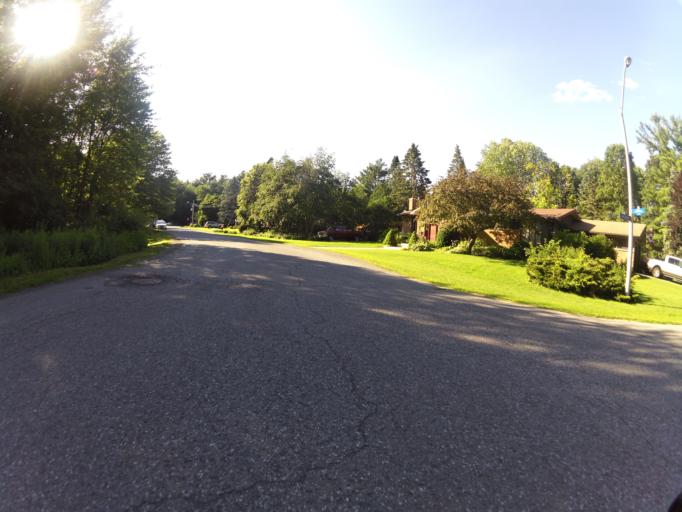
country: CA
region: Ontario
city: Bells Corners
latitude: 45.3156
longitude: -75.7300
